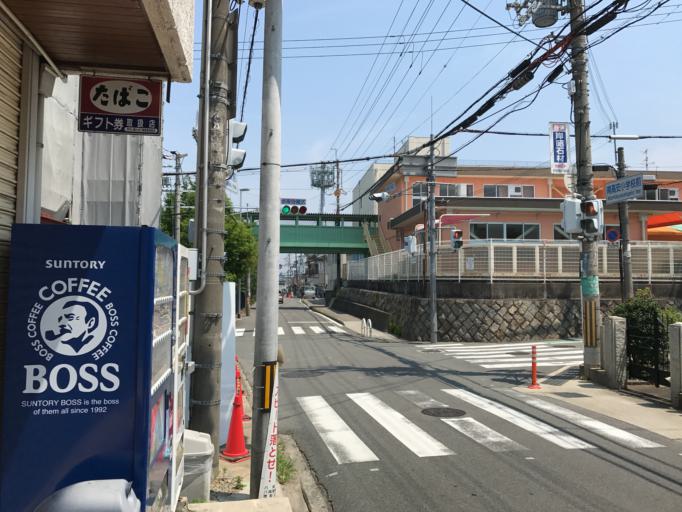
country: JP
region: Osaka
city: Kashihara
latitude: 34.6098
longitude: 135.6325
